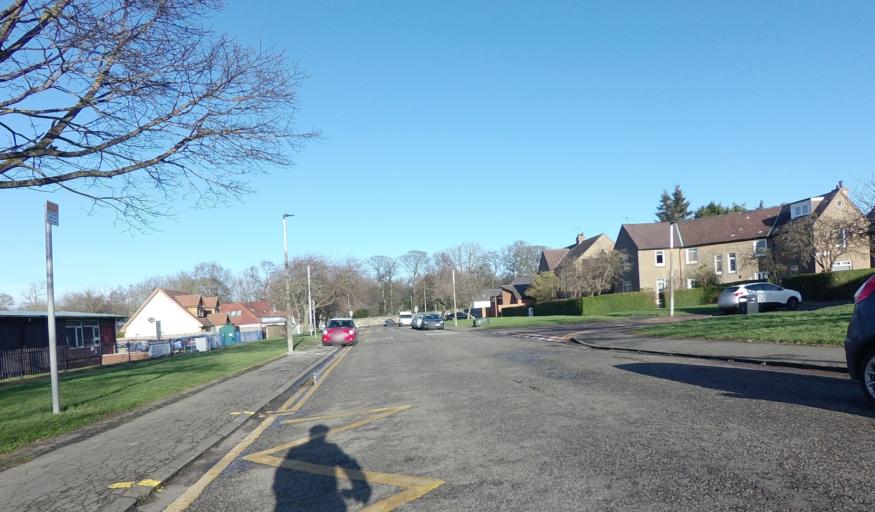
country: GB
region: Scotland
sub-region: Edinburgh
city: Colinton
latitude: 55.9602
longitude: -3.2895
